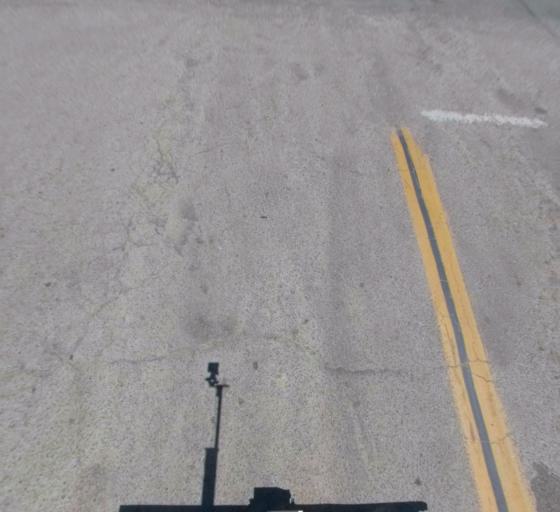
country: US
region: California
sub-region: Madera County
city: Parkwood
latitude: 36.8658
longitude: -120.1104
